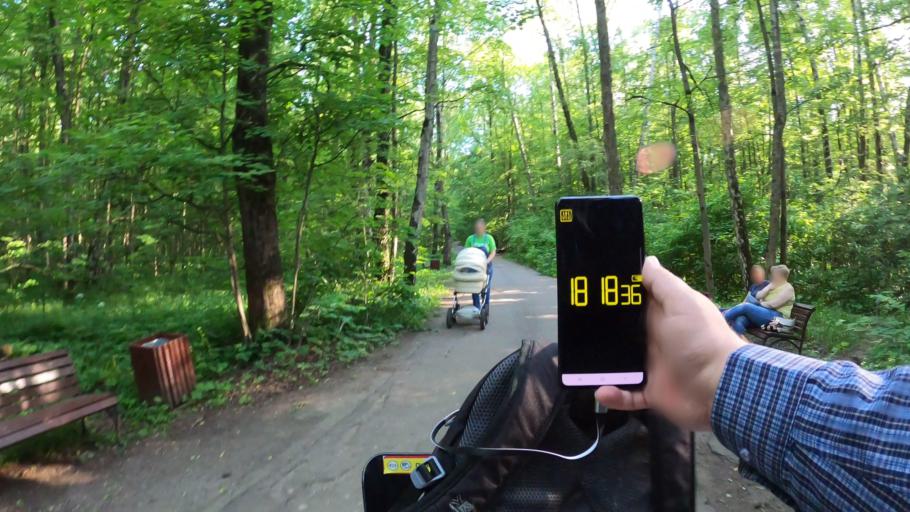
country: RU
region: Moscow
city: Zyuzino
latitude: 55.6199
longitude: 37.5611
